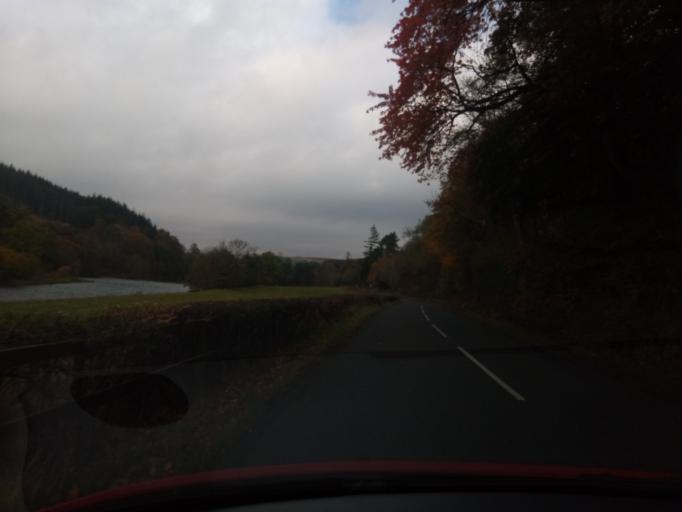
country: GB
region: Scotland
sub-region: The Scottish Borders
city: Selkirk
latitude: 55.6008
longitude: -2.8690
